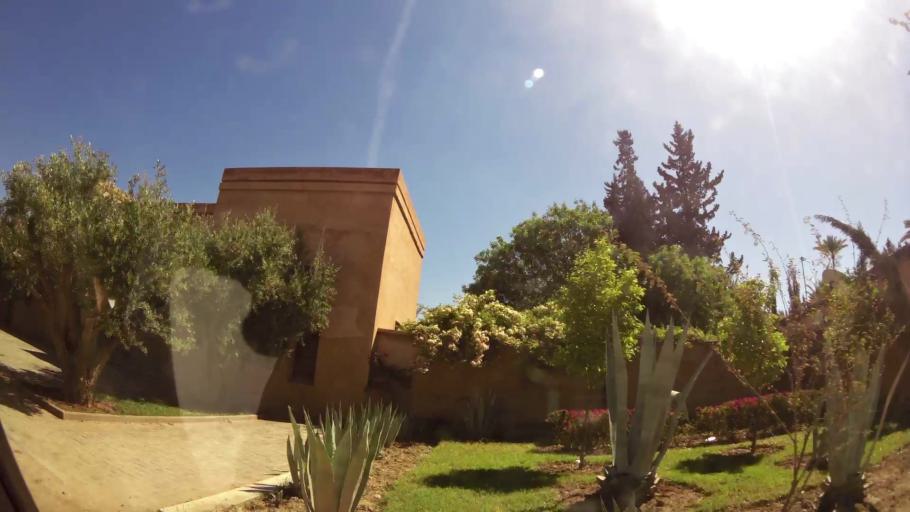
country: MA
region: Marrakech-Tensift-Al Haouz
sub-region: Marrakech
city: Marrakesh
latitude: 31.6686
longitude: -7.9597
